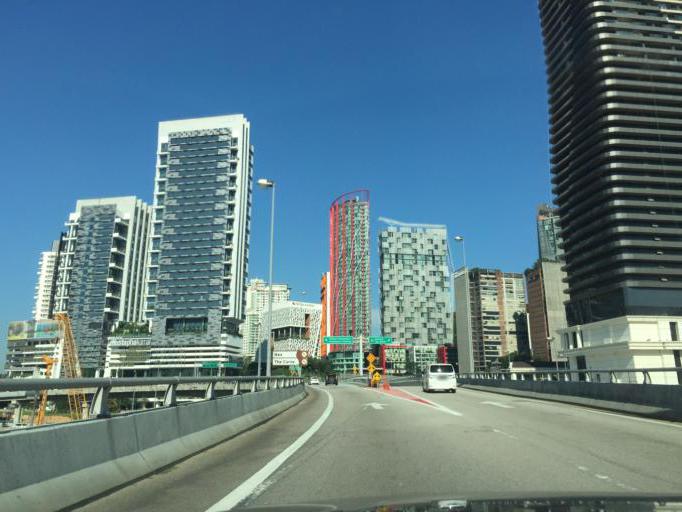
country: MY
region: Selangor
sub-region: Petaling
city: Petaling Jaya
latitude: 3.1651
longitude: 101.6172
